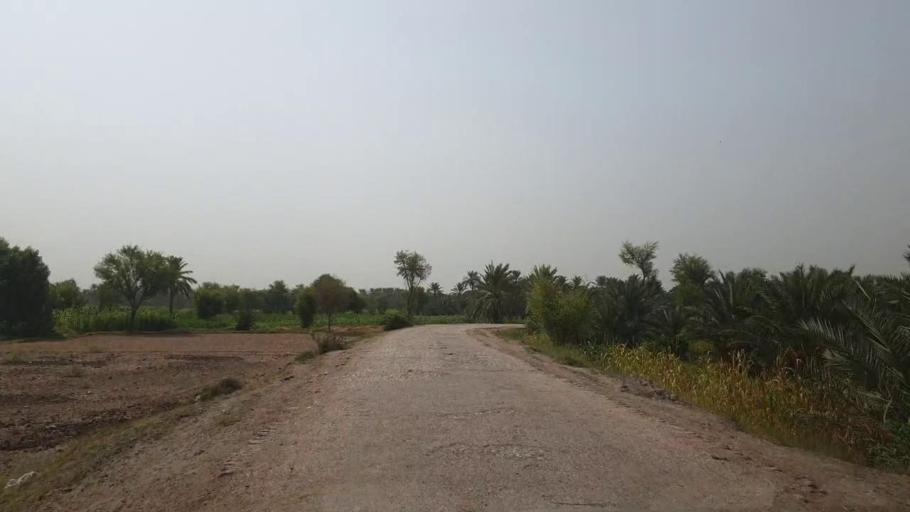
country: PK
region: Sindh
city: Gambat
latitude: 27.4107
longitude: 68.5529
